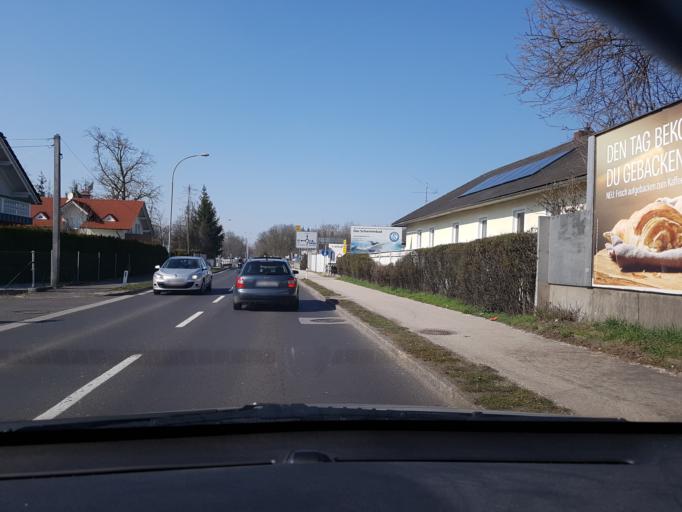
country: AT
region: Upper Austria
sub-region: Politischer Bezirk Linz-Land
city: Traun
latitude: 48.2075
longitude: 14.2462
